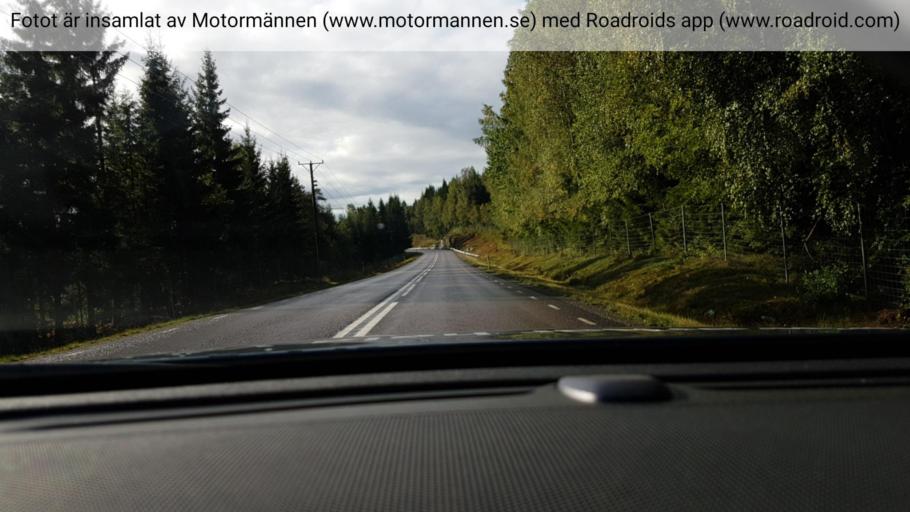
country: SE
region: Vaestra Goetaland
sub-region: Harryda Kommun
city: Hindas
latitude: 57.6443
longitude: 12.4063
